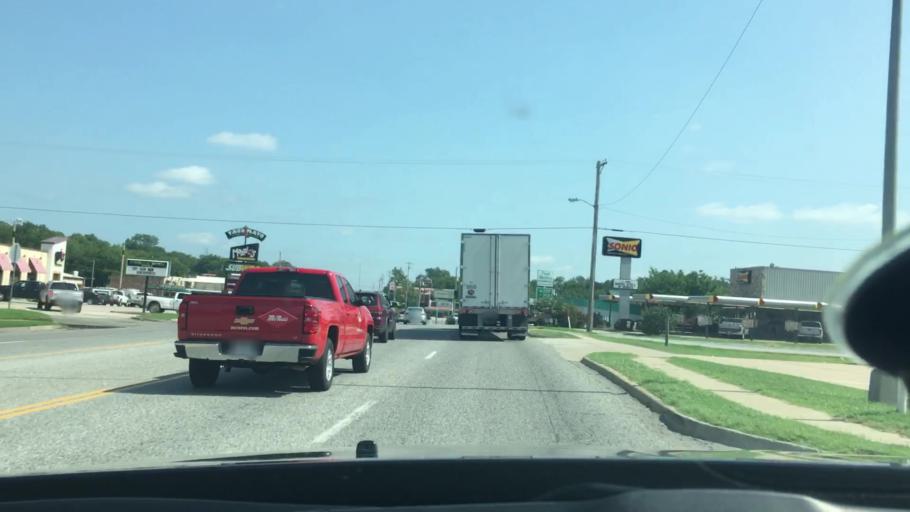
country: US
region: Oklahoma
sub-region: Atoka County
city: Atoka
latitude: 34.3796
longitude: -96.1310
